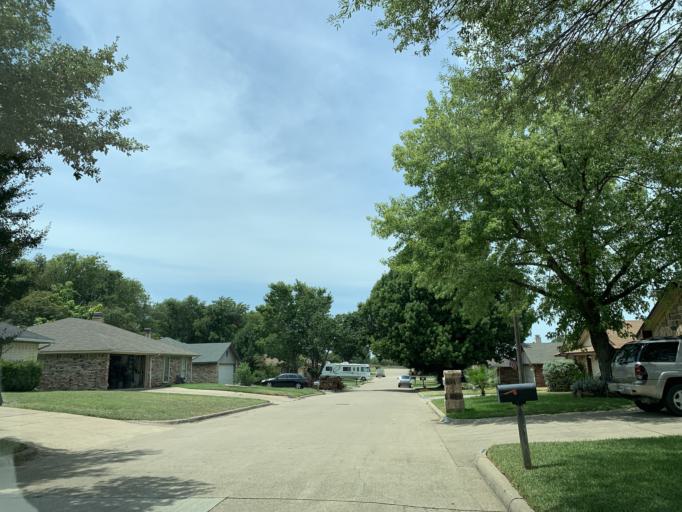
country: US
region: Texas
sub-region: Dallas County
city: Grand Prairie
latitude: 32.6635
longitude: -97.0257
